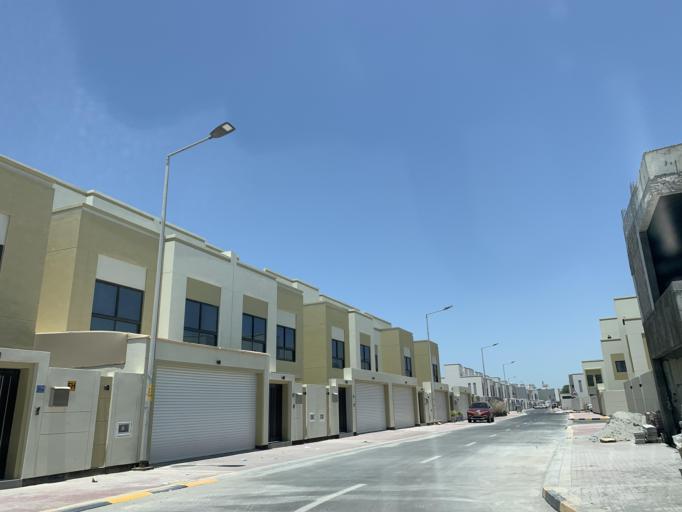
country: BH
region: Manama
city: Jidd Hafs
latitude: 26.2326
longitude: 50.4951
